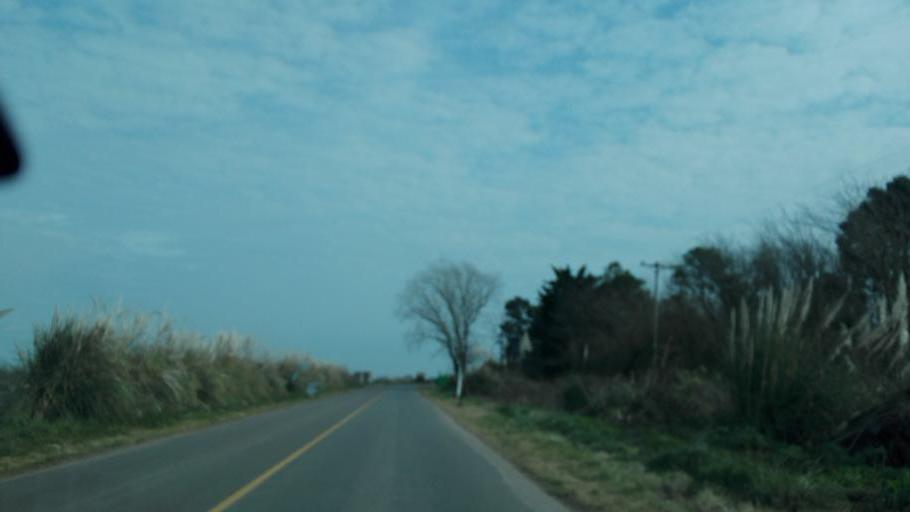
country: AR
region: Buenos Aires
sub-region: Partido de Chascomus
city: Chascomus
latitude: -35.5531
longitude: -58.0530
